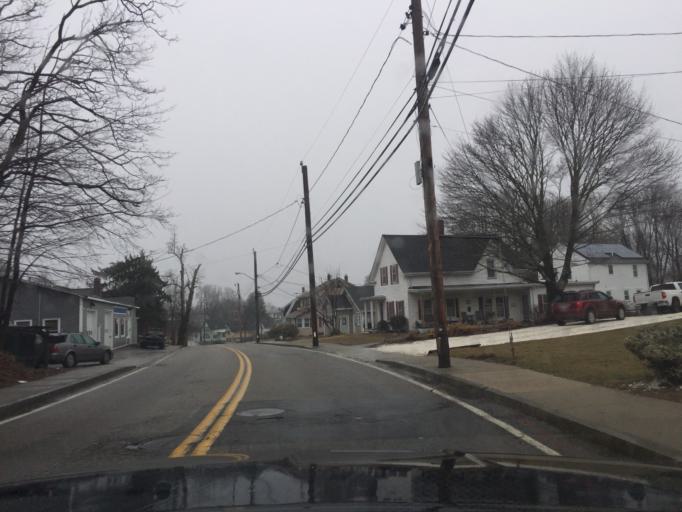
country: US
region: Massachusetts
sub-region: Plymouth County
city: Plymouth
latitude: 41.9492
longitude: -70.6594
